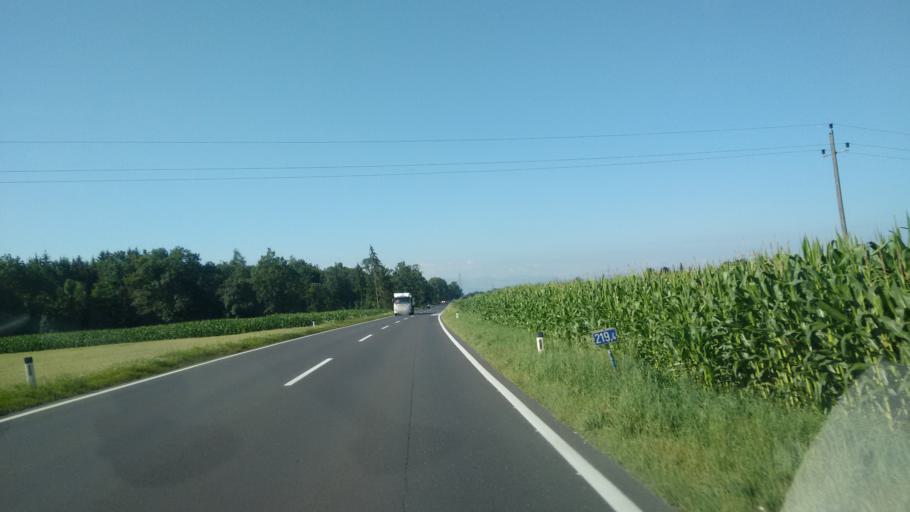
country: AT
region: Upper Austria
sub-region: Wels-Land
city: Gunskirchen
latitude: 48.1130
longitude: 13.9325
